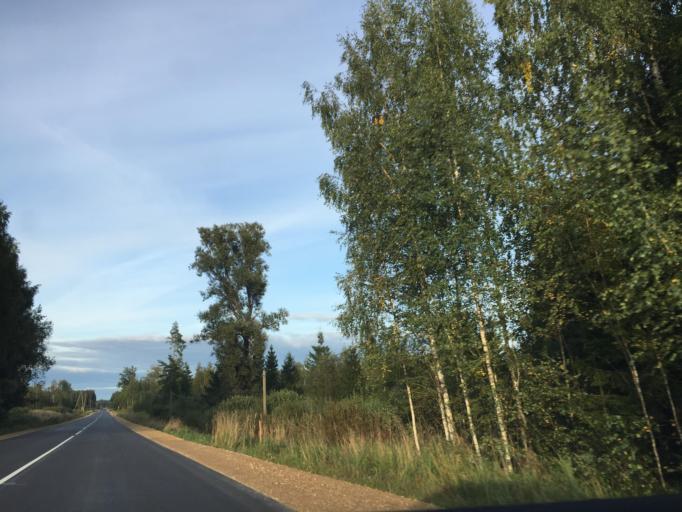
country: LV
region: Viesite
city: Viesite
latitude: 56.3530
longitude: 25.5967
